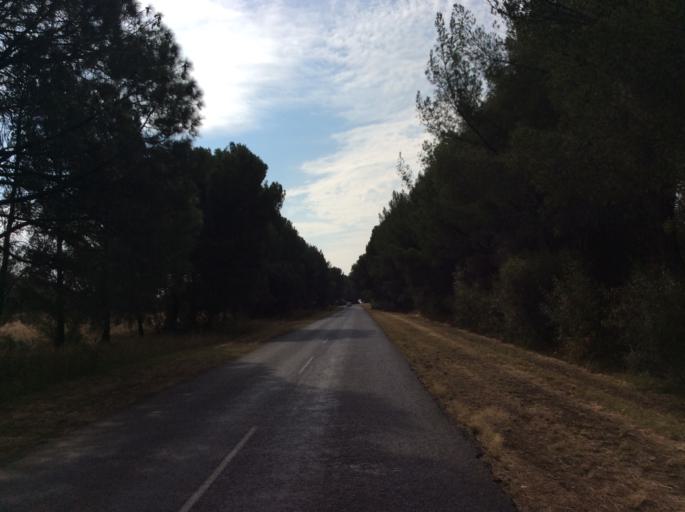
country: ZA
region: Orange Free State
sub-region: Xhariep District Municipality
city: Dewetsdorp
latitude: -29.5738
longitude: 26.6649
